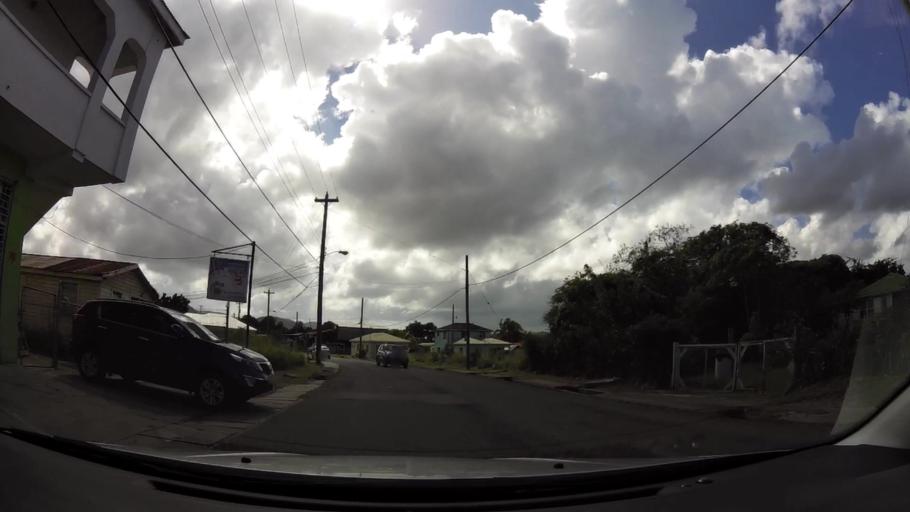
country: AG
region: Saint John
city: Saint John's
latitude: 17.1061
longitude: -61.8354
